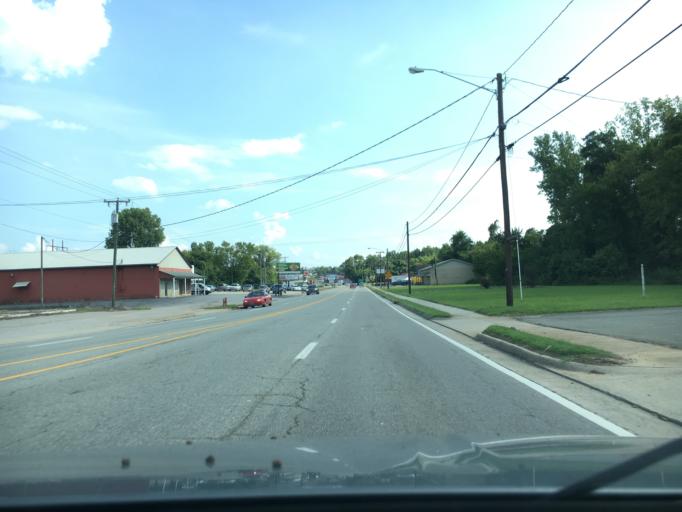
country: US
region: Virginia
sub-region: Halifax County
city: South Boston
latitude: 36.6928
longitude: -78.9006
